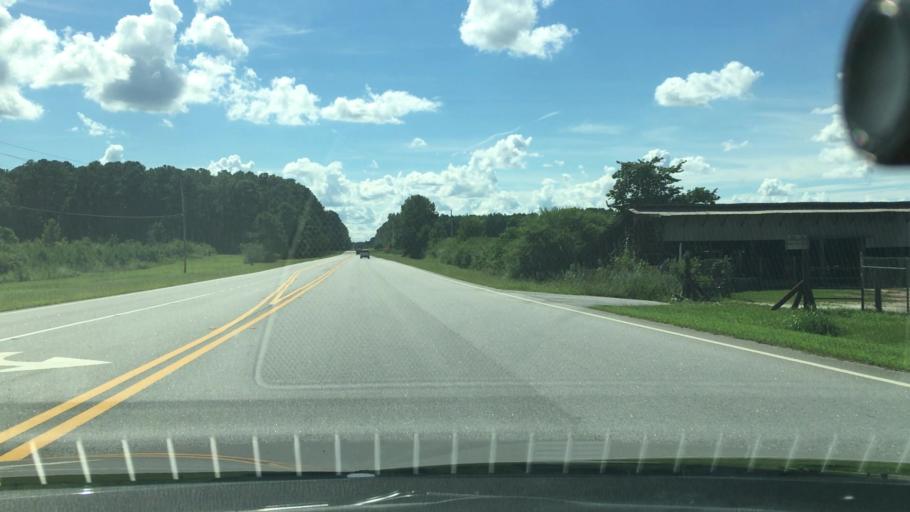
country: US
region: Georgia
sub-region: Butts County
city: Jackson
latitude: 33.2903
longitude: -84.0016
